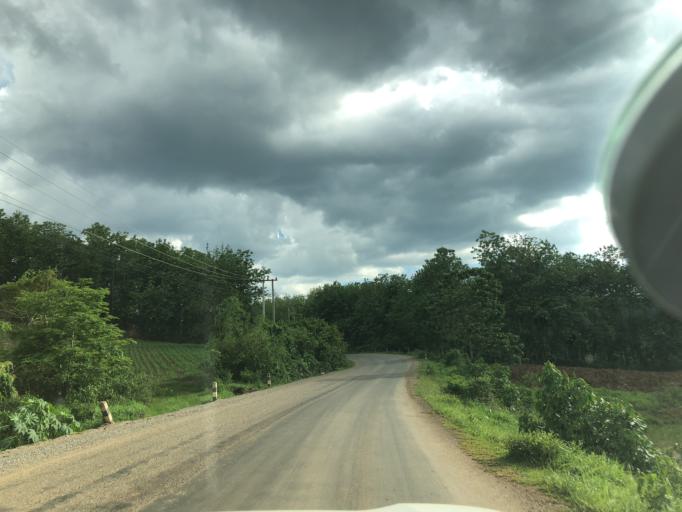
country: TH
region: Uttaradit
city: Ban Khok
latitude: 18.1265
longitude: 101.3736
